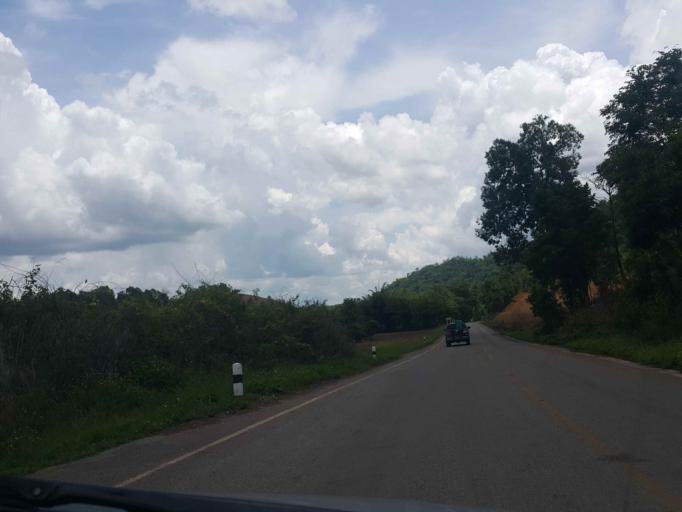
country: TH
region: Phayao
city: Chiang Muan
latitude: 18.8998
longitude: 100.1332
